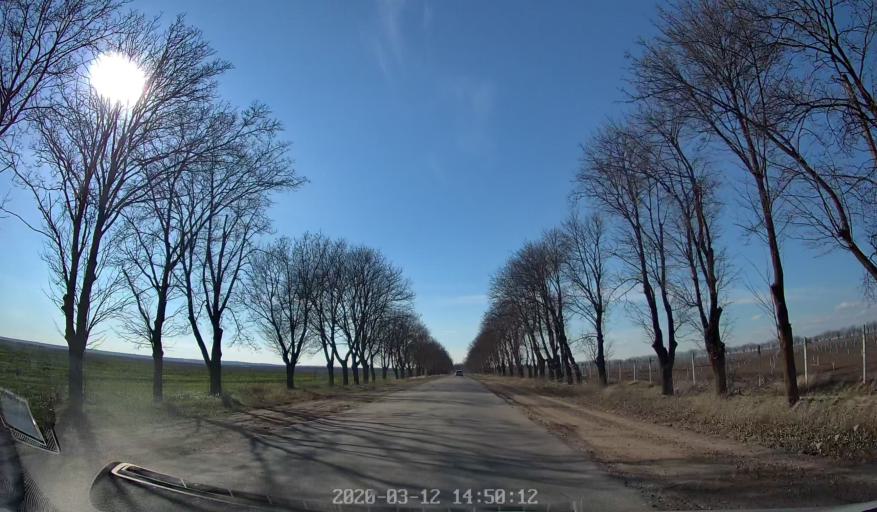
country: MD
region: Criuleni
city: Criuleni
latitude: 47.2229
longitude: 29.1342
